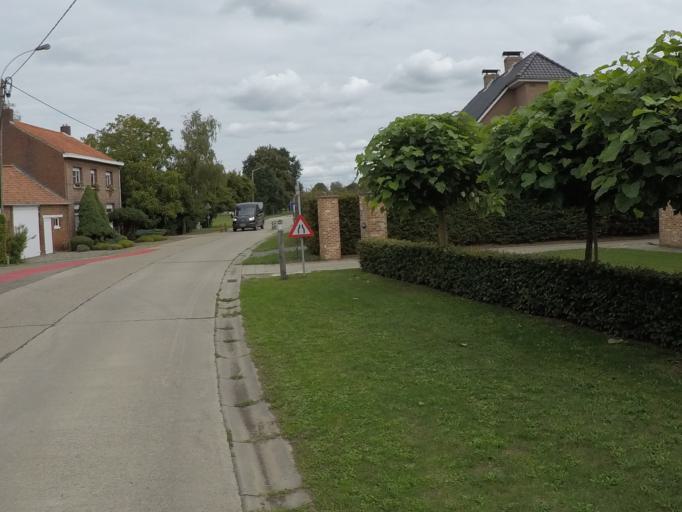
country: BE
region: Flanders
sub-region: Provincie Antwerpen
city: Zandhoven
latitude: 51.2227
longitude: 4.6990
